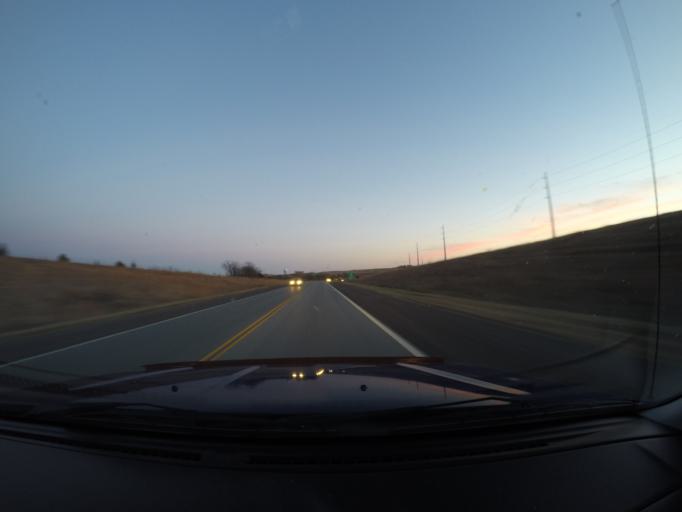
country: US
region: Kansas
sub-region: Douglas County
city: Lawrence
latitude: 38.9846
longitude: -95.3385
